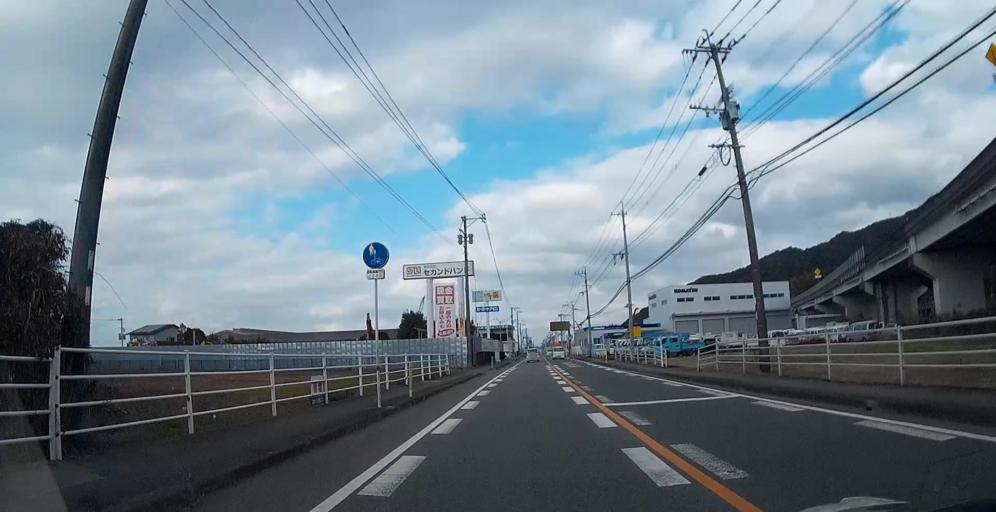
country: JP
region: Kumamoto
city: Yatsushiro
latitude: 32.4661
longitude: 130.6042
